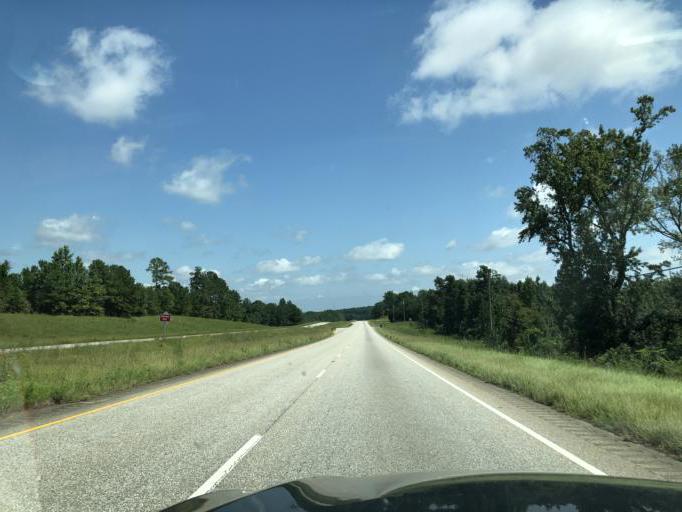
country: US
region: Alabama
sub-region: Henry County
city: Abbeville
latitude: 31.7219
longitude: -85.2653
